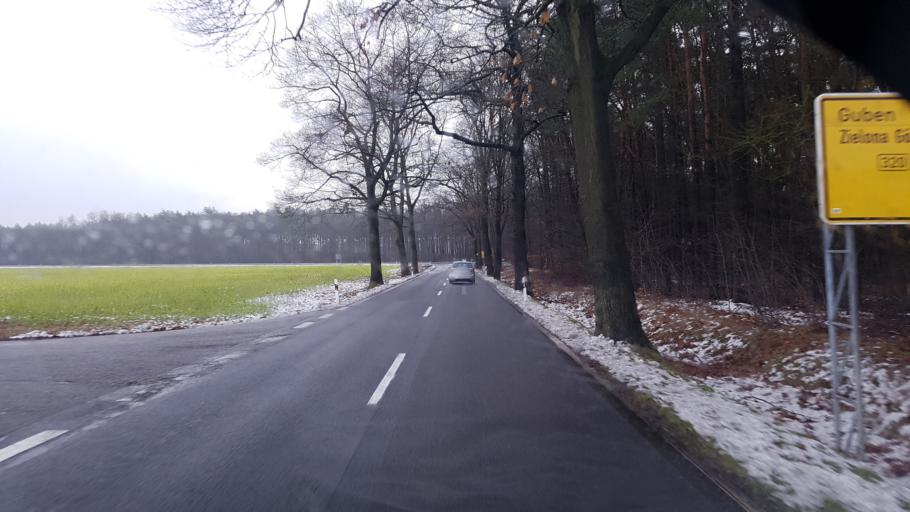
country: DE
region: Brandenburg
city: Schenkendobern
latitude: 51.9518
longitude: 14.5950
